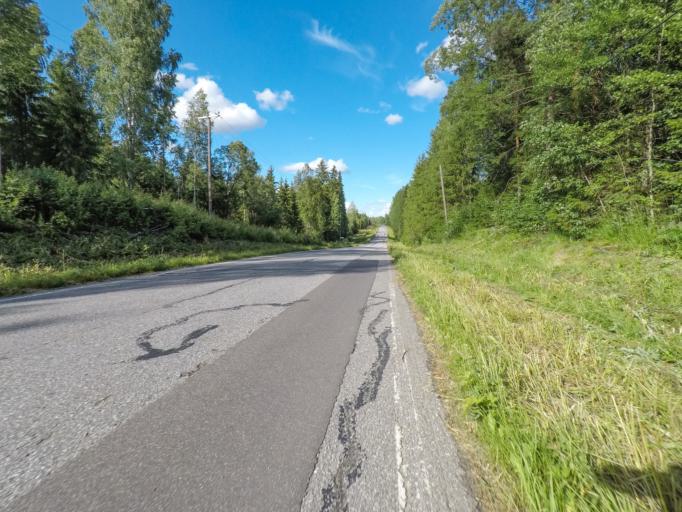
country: FI
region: South Karelia
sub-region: Imatra
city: Imatra
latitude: 61.1352
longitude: 28.7324
